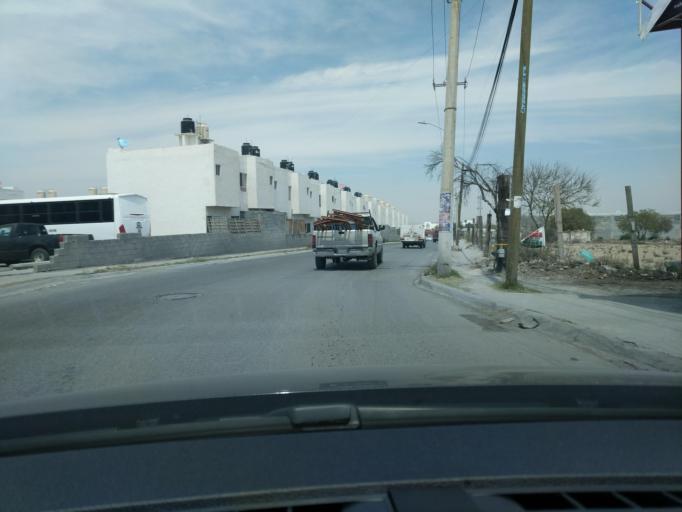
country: MX
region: Coahuila
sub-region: Arteaga
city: Arteaga
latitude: 25.4290
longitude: -100.9123
